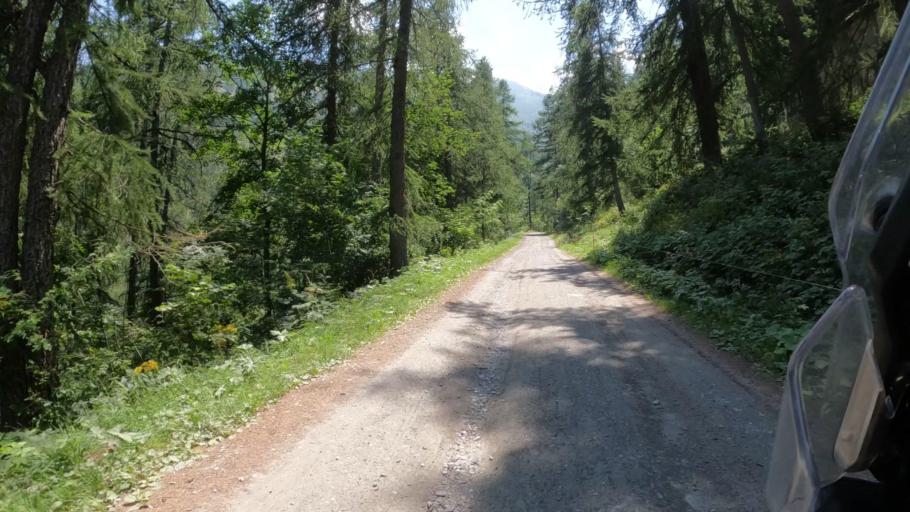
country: IT
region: Piedmont
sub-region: Provincia di Torino
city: Meana di Susa
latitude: 45.0957
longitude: 7.0604
